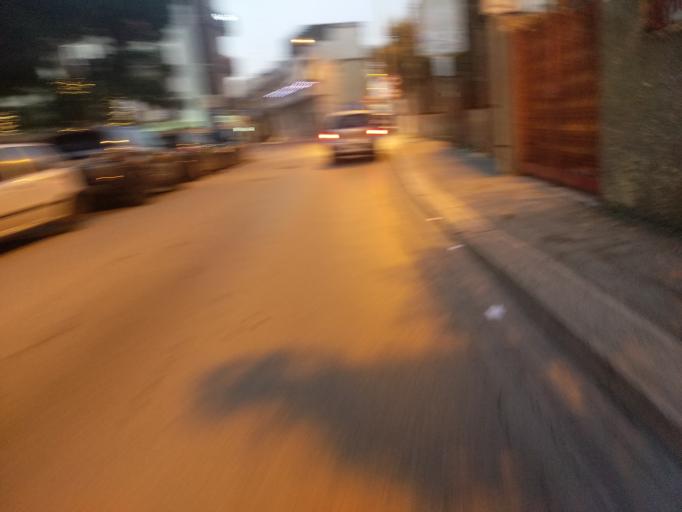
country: IT
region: Apulia
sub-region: Provincia di Bari
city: Modugno
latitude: 41.0787
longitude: 16.7809
